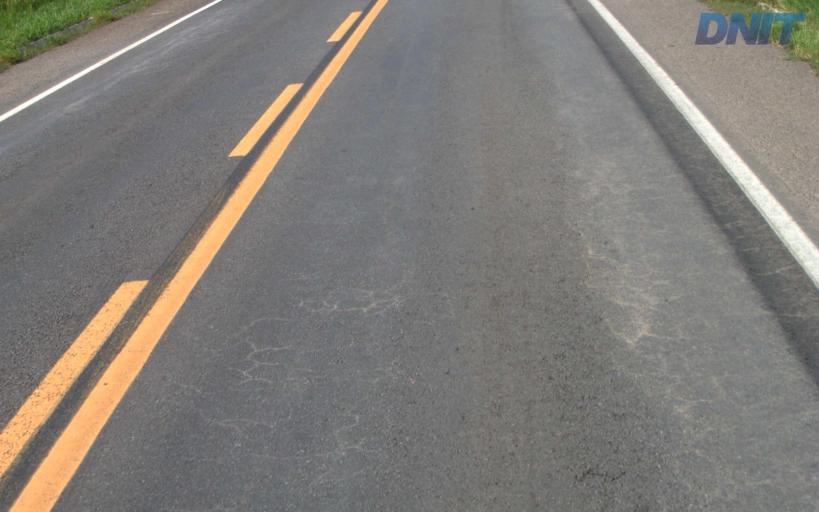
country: BR
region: Minas Gerais
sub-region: Belo Oriente
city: Belo Oriente
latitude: -19.1781
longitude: -42.2575
